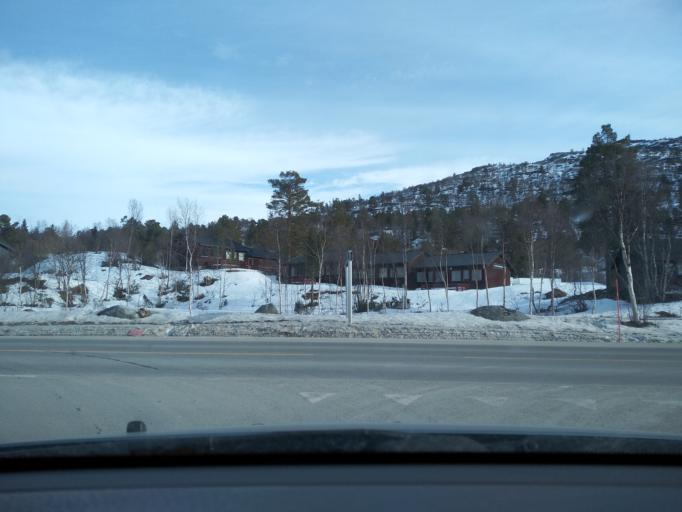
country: NO
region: Aust-Agder
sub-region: Bykle
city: Hovden
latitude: 59.5564
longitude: 7.3601
